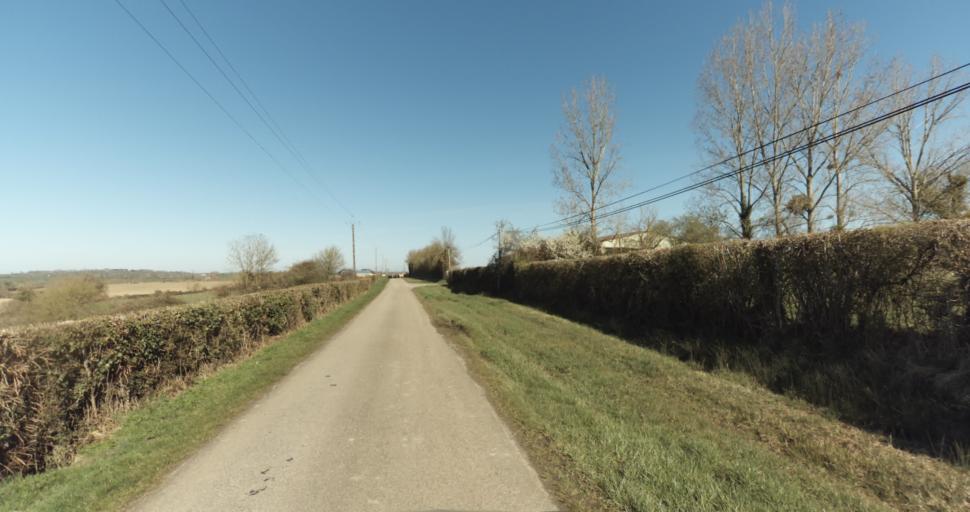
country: FR
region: Lower Normandy
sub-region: Departement de l'Orne
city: Trun
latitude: 48.9345
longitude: 0.0413
